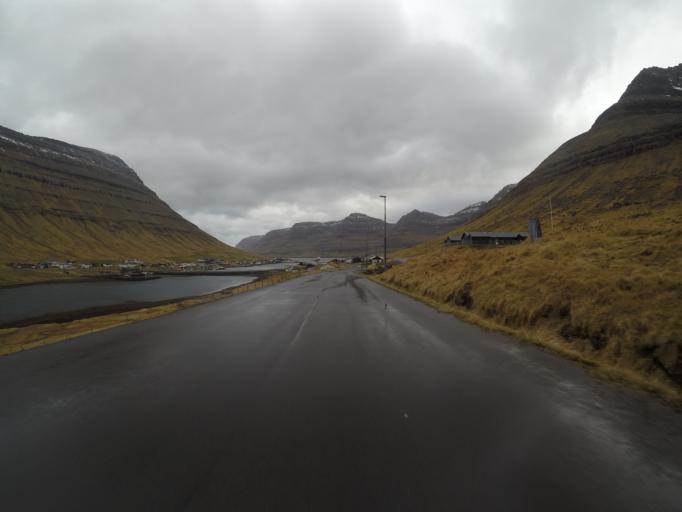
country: FO
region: Nordoyar
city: Klaksvik
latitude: 62.3016
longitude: -6.5321
